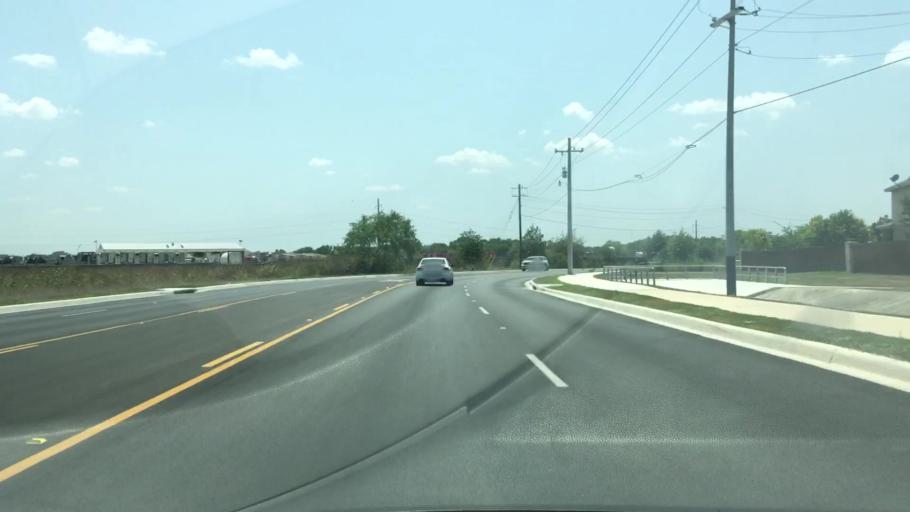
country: US
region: Texas
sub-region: Guadalupe County
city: Cibolo
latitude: 29.5708
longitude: -98.2411
